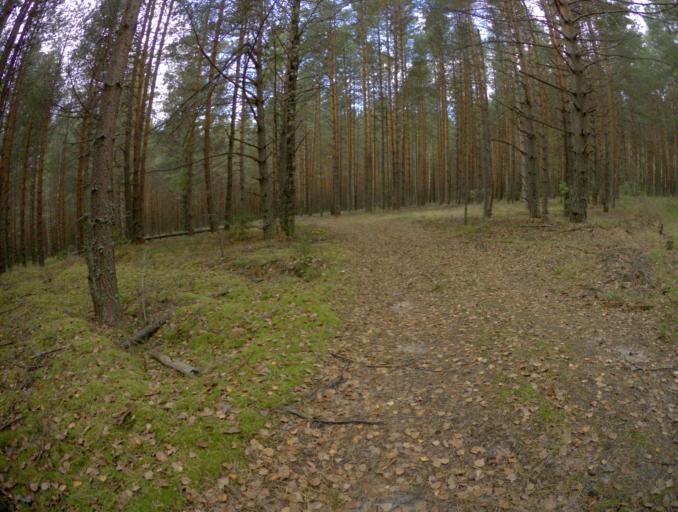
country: RU
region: Vladimir
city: Golovino
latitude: 55.8804
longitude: 40.4369
